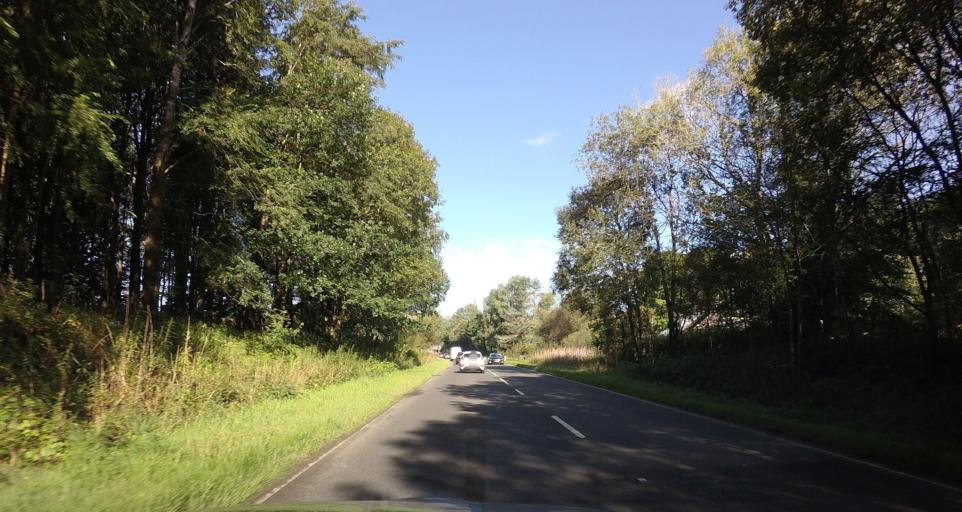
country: GB
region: Scotland
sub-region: Stirling
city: Callander
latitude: 56.2323
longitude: -4.1780
